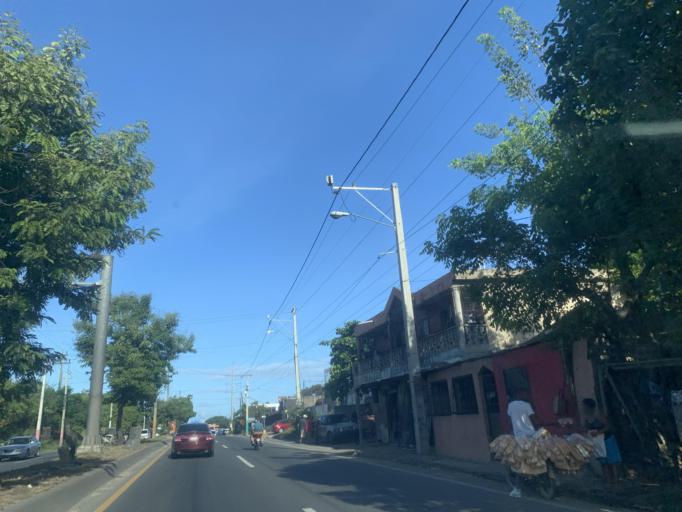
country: DO
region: San Cristobal
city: El Carril
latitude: 18.4306
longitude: -70.0045
